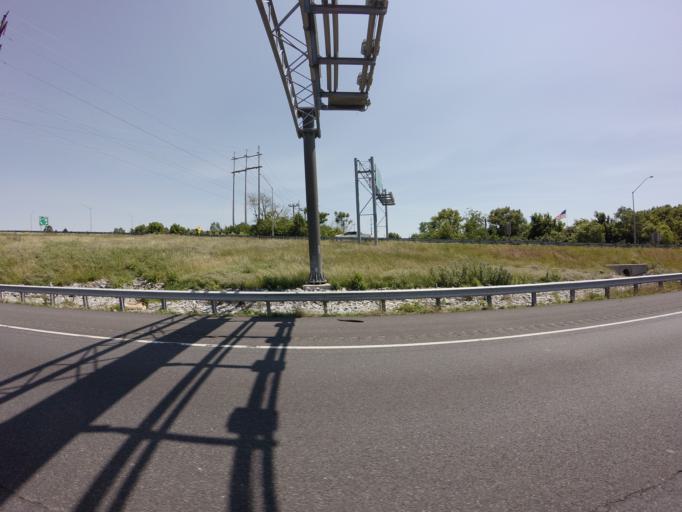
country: US
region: Maryland
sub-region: Frederick County
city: Frederick
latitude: 39.4008
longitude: -77.4053
